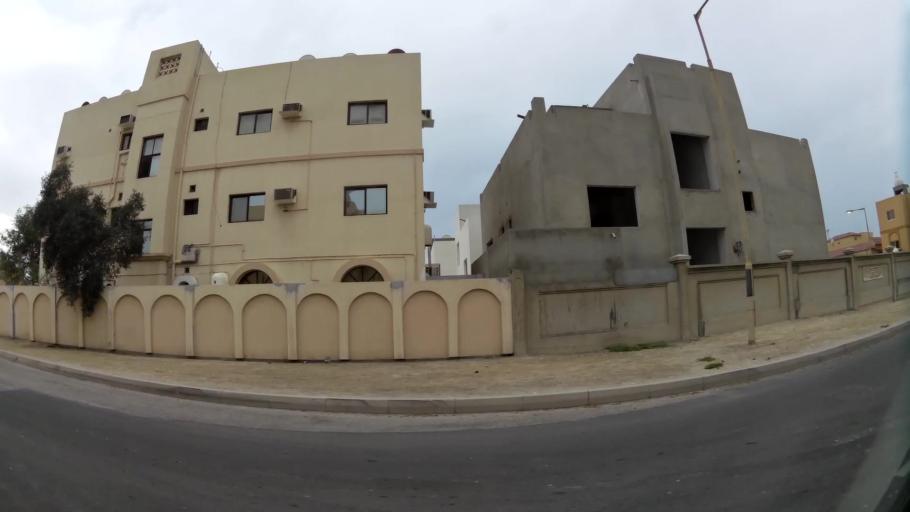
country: BH
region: Central Governorate
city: Madinat Hamad
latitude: 26.1092
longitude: 50.4994
